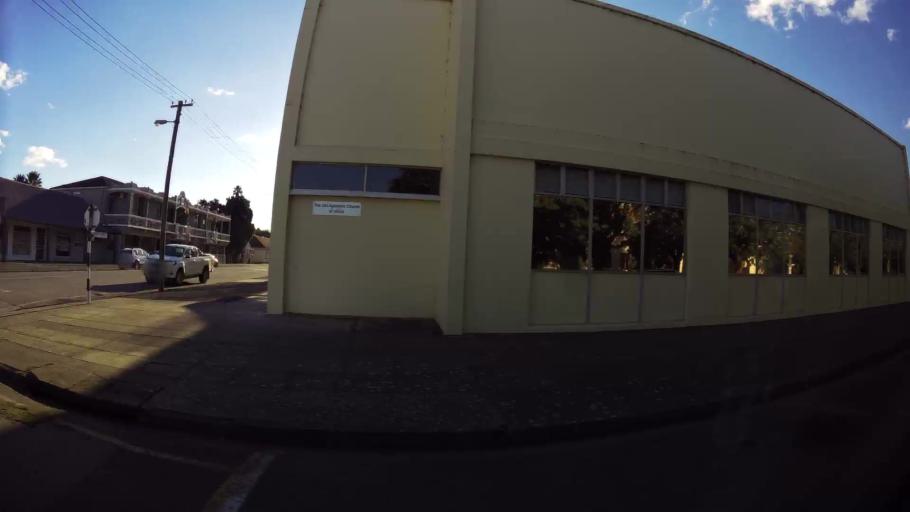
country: ZA
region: Western Cape
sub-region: Eden District Municipality
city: Riversdale
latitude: -34.0894
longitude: 20.9575
